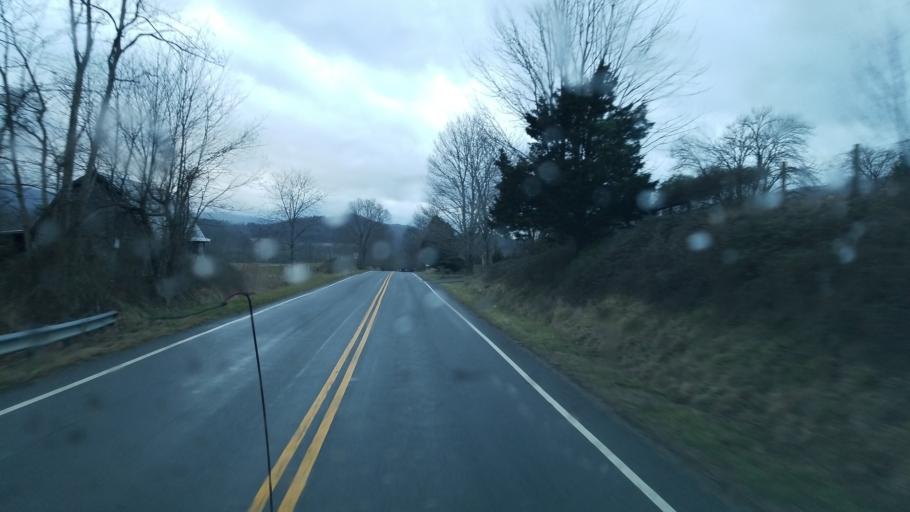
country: US
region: Virginia
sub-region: Giles County
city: Narrows
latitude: 37.2005
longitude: -80.8233
